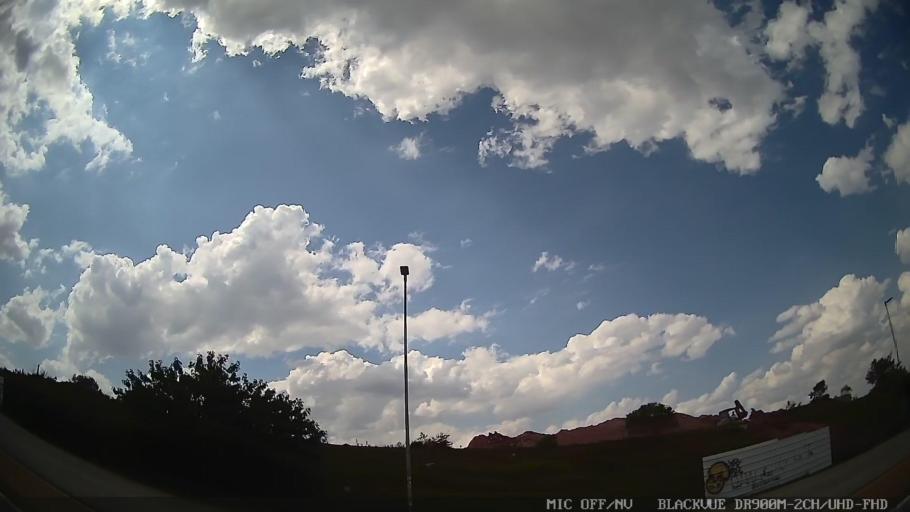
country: BR
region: Sao Paulo
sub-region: Ferraz De Vasconcelos
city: Ferraz de Vasconcelos
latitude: -23.5460
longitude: -46.4697
